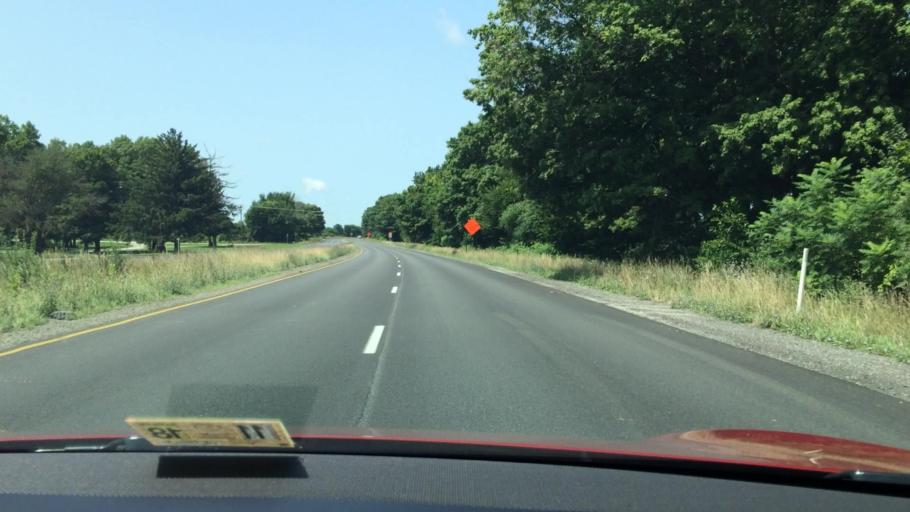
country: US
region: Indiana
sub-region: LaPorte County
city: Hudson Lake
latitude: 41.6722
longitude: -86.5998
